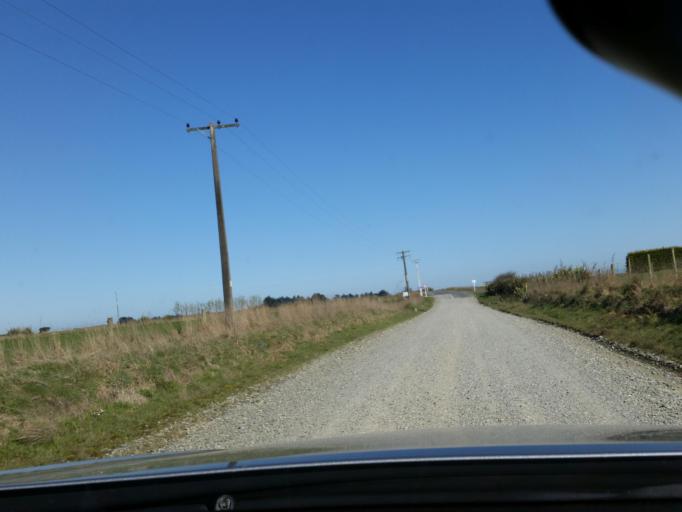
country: NZ
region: Southland
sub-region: Southland District
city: Winton
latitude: -46.2508
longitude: 168.4569
